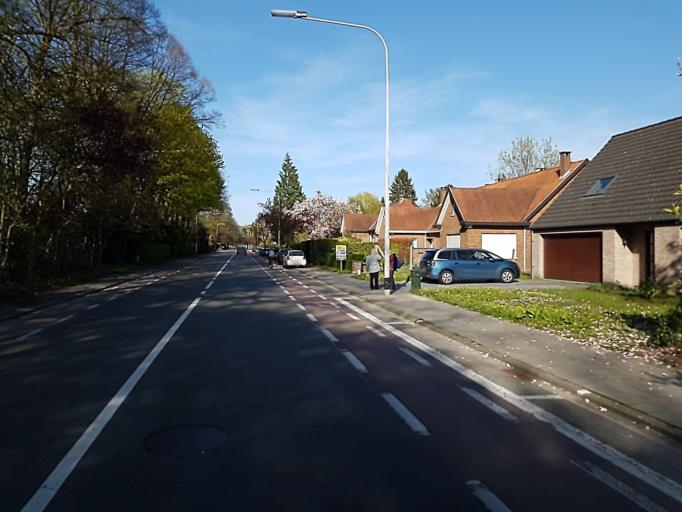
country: BE
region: Flanders
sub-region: Provincie Vlaams-Brabant
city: Sint-Genesius-Rode
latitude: 50.7504
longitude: 4.3663
